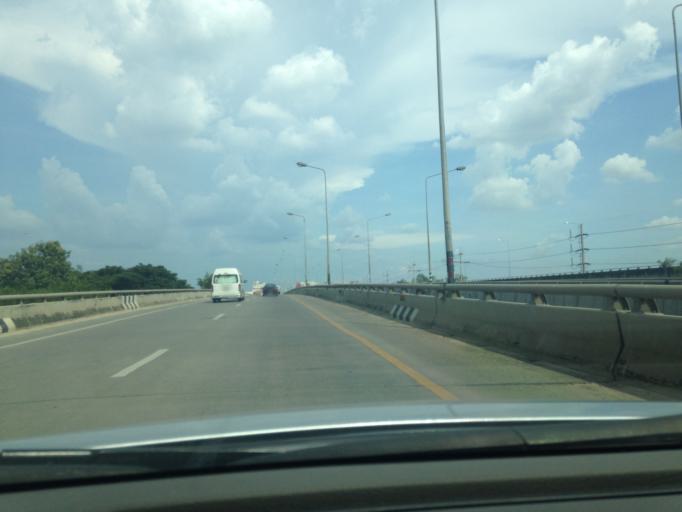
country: TH
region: Pathum Thani
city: Khlong Luang
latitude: 14.0661
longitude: 100.5886
